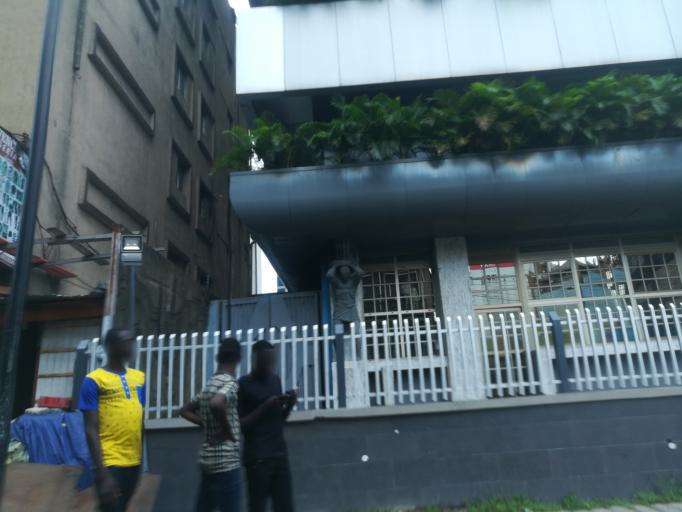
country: NG
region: Lagos
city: Lagos
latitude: 6.4545
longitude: 3.3863
